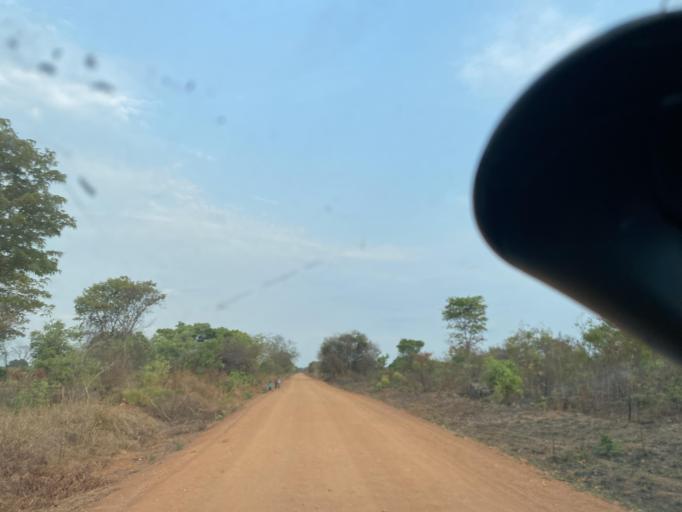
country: ZM
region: Lusaka
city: Chongwe
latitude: -15.2203
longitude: 28.5823
